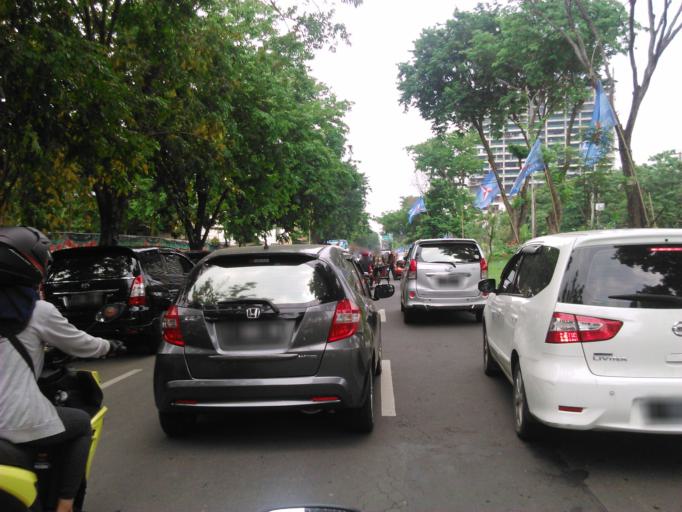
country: ID
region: East Java
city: Mulyorejo
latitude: -7.2802
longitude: 112.7843
